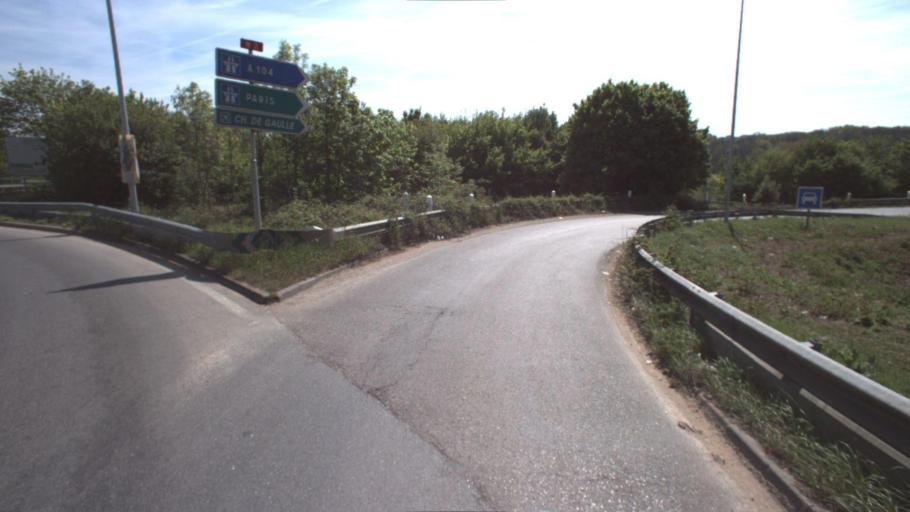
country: FR
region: Ile-de-France
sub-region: Departement de Seine-et-Marne
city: Saint-Mard
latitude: 49.0579
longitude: 2.7004
